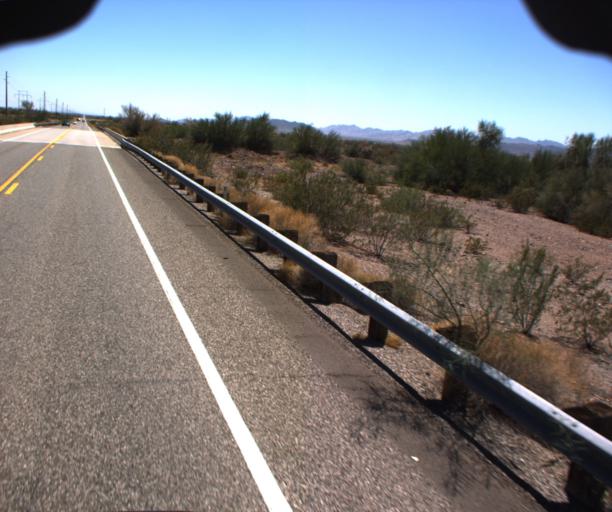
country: US
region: Arizona
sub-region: La Paz County
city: Quartzsite
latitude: 33.7472
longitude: -114.2171
